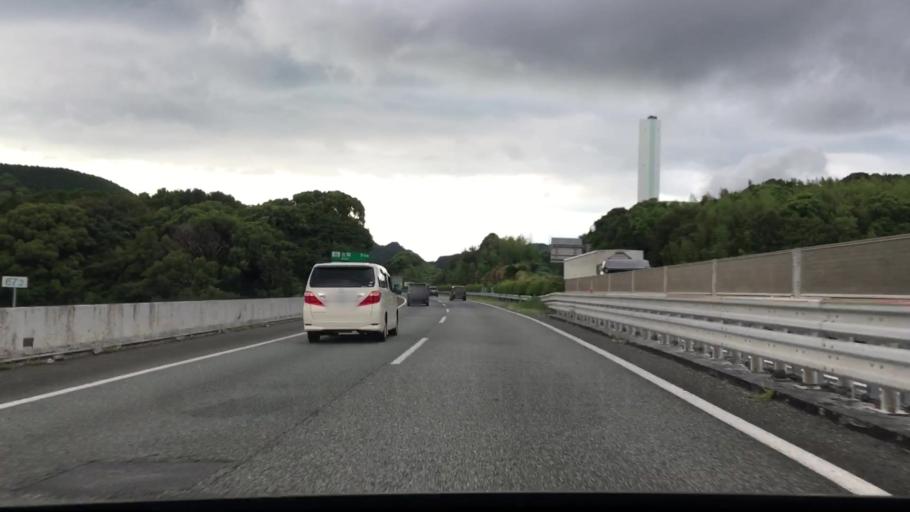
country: JP
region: Fukuoka
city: Sasaguri
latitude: 33.6392
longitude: 130.4891
